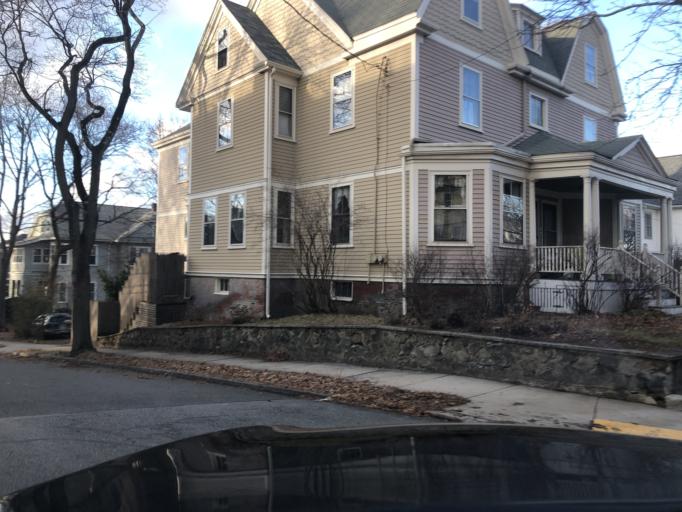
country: US
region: Massachusetts
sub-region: Middlesex County
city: Arlington
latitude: 42.4150
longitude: -71.1609
